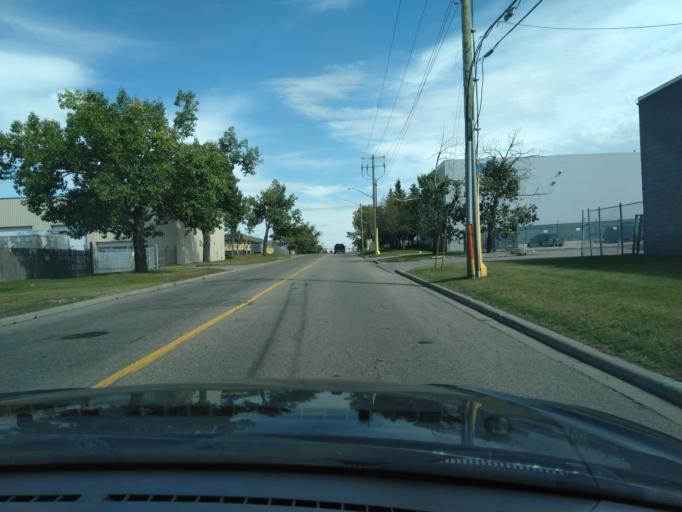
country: CA
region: Alberta
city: Calgary
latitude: 51.0769
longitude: -114.0163
